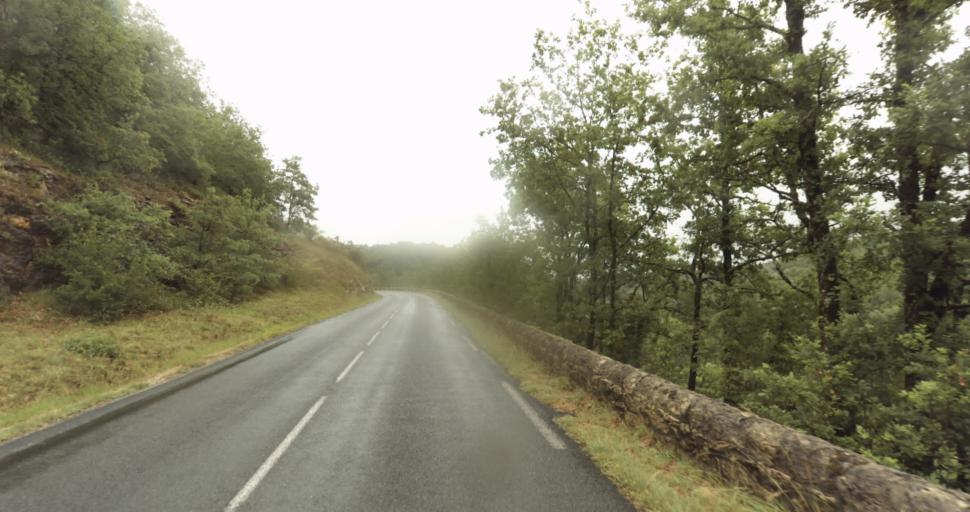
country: FR
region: Aquitaine
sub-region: Departement de la Dordogne
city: Beaumont-du-Perigord
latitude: 44.7709
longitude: 0.8083
